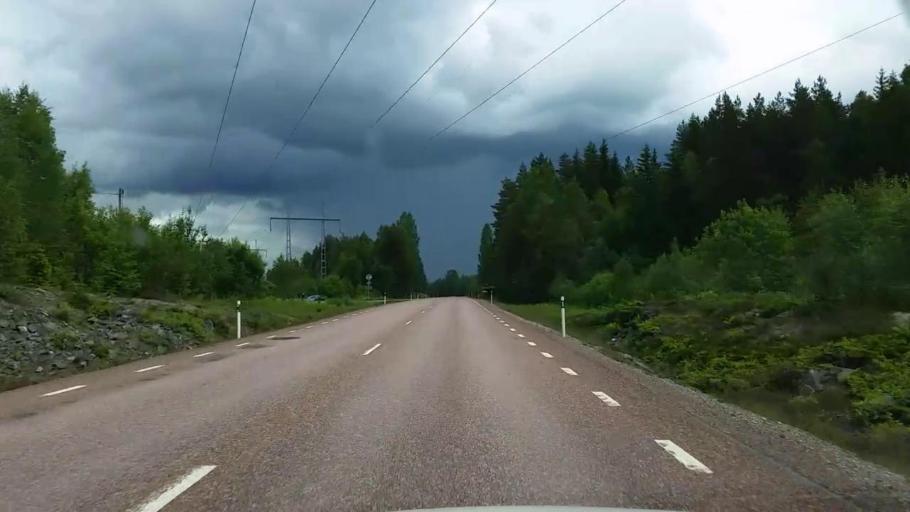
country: SE
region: Gaevleborg
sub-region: Hofors Kommun
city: Hofors
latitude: 60.5451
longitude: 16.4692
